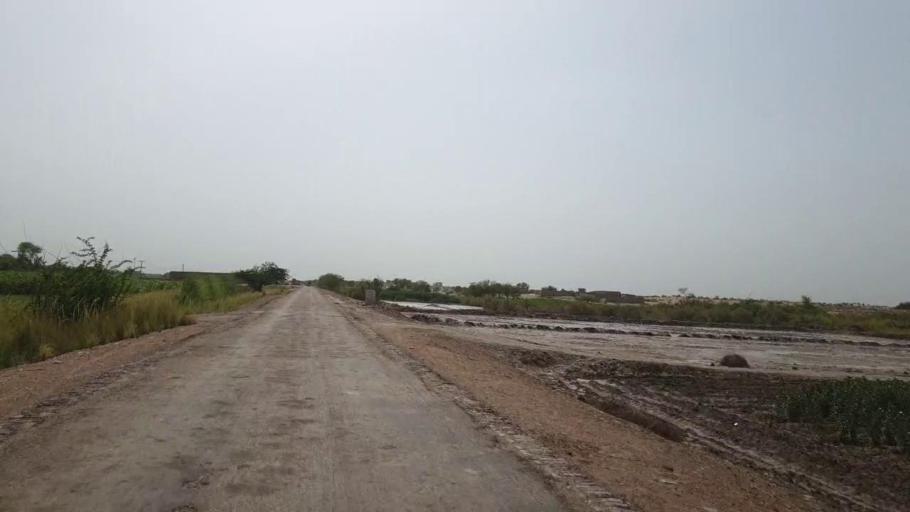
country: PK
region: Sindh
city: Bandhi
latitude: 26.5386
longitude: 68.3988
